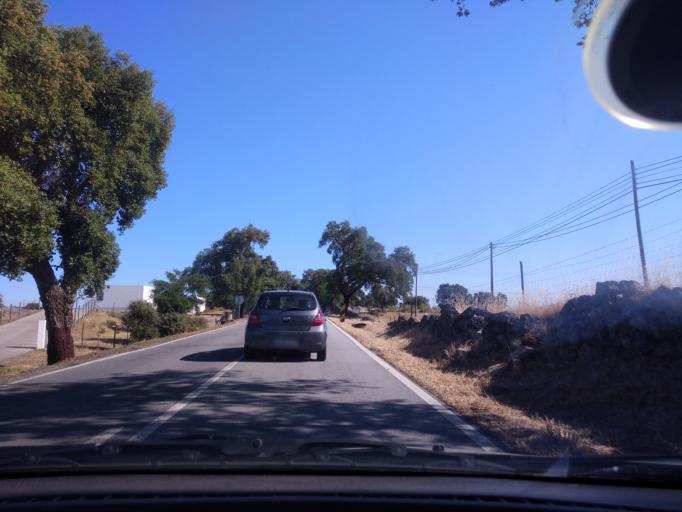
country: PT
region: Portalegre
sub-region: Nisa
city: Nisa
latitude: 39.5041
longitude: -7.6438
